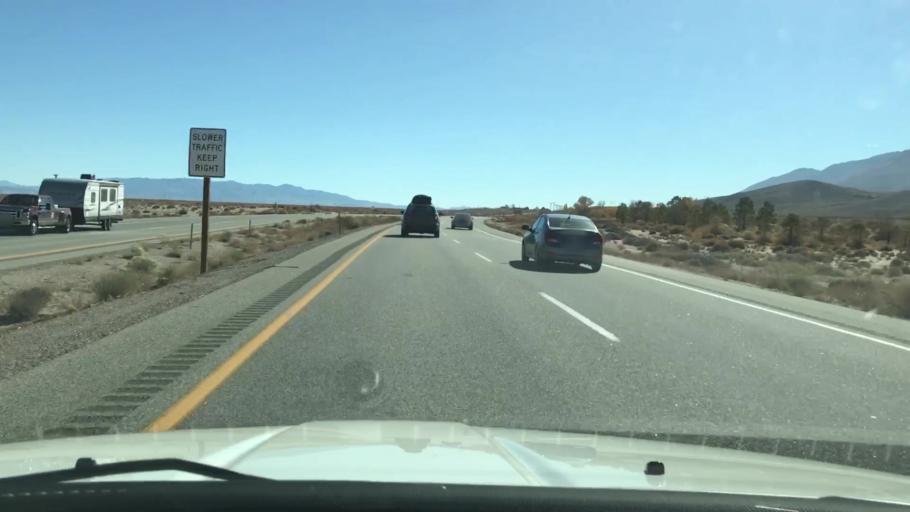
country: US
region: California
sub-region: Inyo County
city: Lone Pine
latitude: 36.5651
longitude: -118.0521
